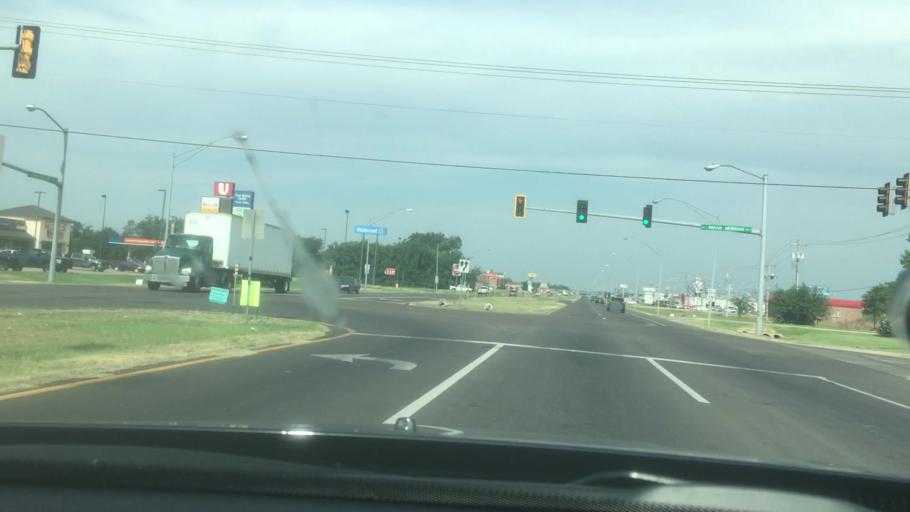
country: US
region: Oklahoma
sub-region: Garvin County
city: Pauls Valley
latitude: 34.7393
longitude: -97.2473
